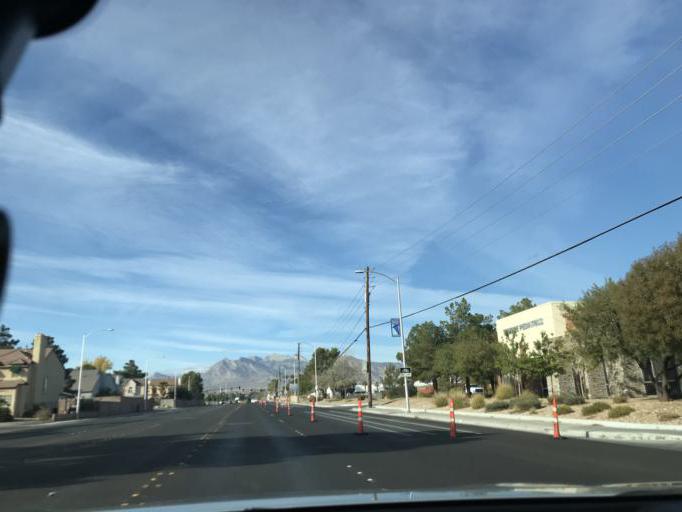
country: US
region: Nevada
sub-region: Clark County
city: Spring Valley
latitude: 36.2035
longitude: -115.2484
